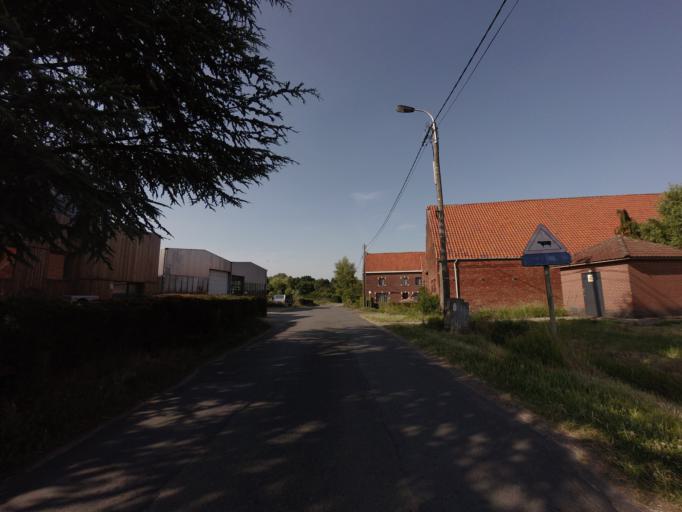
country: BE
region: Flanders
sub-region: Provincie Antwerpen
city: Kontich
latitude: 51.1012
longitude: 4.4630
